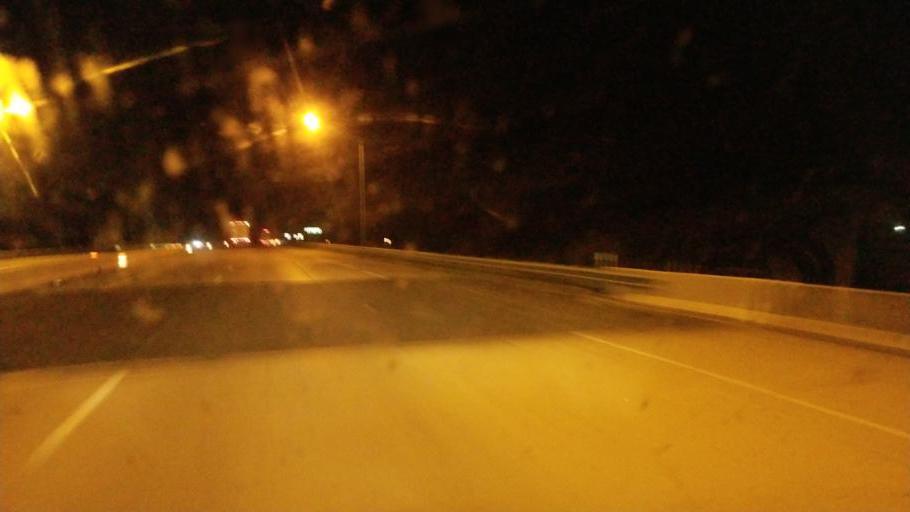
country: US
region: Indiana
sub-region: Allen County
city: New Haven
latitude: 41.0917
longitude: -84.9944
